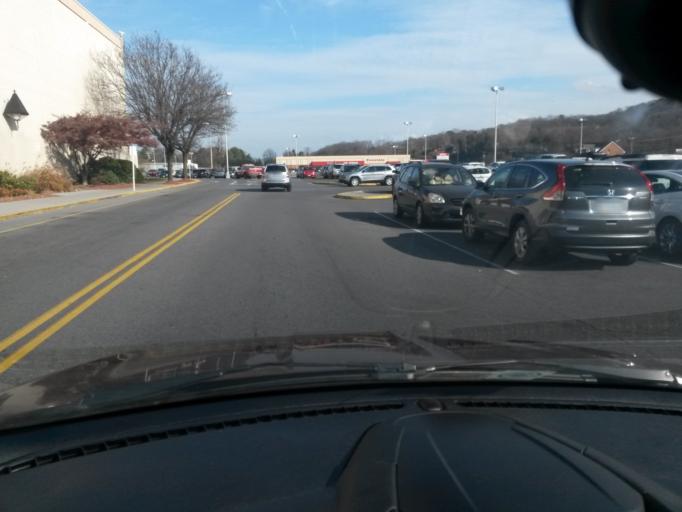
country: US
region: Virginia
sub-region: Roanoke County
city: Narrows
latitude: 37.2300
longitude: -79.9775
